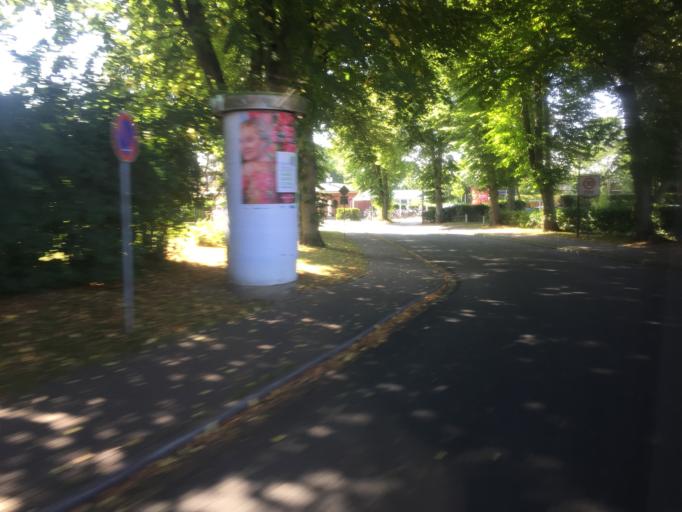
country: DE
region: Schleswig-Holstein
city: Timmendorfer Strand
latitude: 53.9952
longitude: 10.7631
